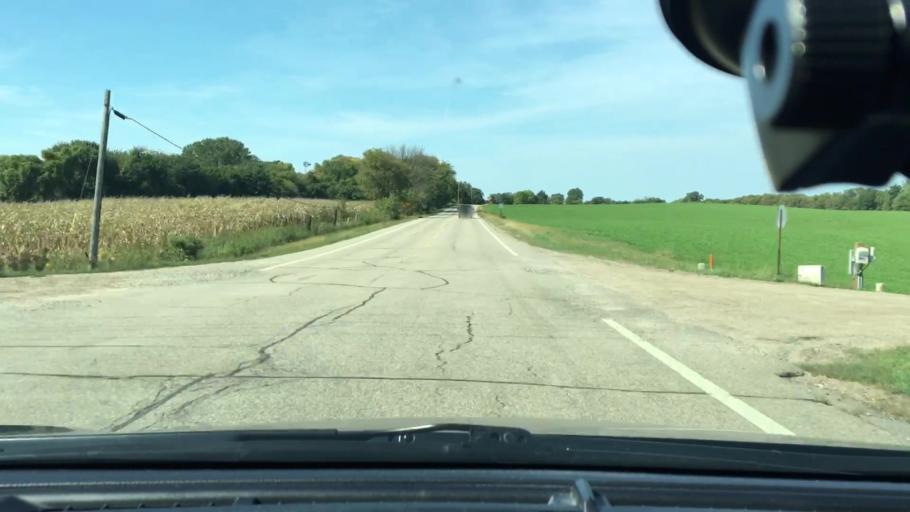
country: US
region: Minnesota
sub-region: Hennepin County
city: Corcoran
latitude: 45.1208
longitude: -93.6052
